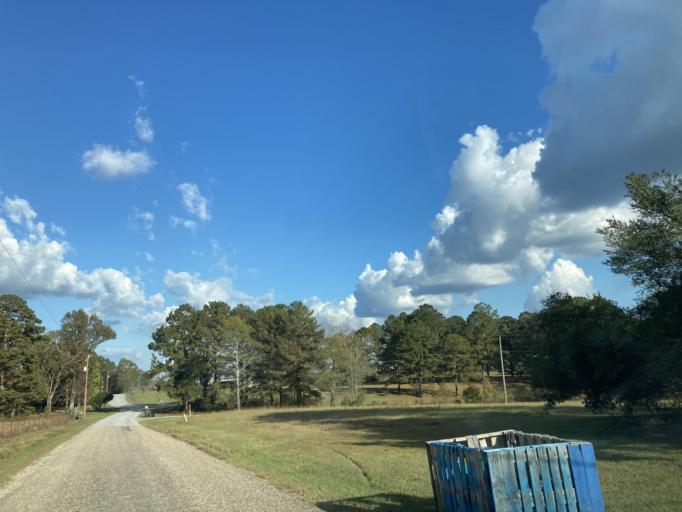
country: US
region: Mississippi
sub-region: Lamar County
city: Sumrall
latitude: 31.4361
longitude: -89.6064
